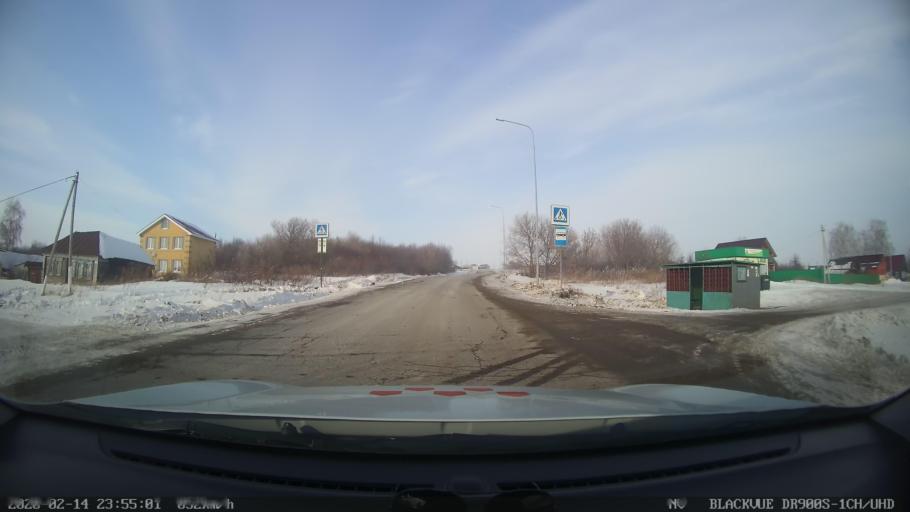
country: RU
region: Tatarstan
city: Kuybyshevskiy Zaton
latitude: 55.3135
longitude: 49.1446
